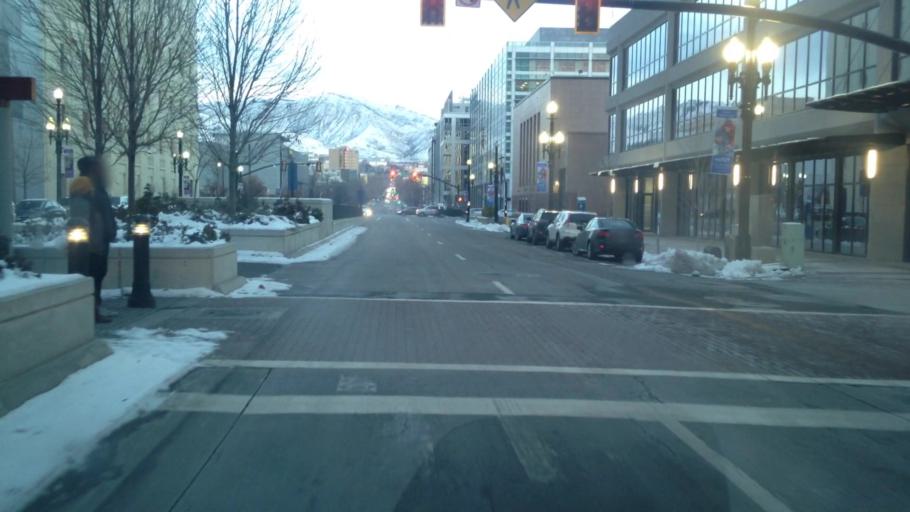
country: US
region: Utah
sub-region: Salt Lake County
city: Salt Lake City
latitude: 40.7671
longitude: -111.8900
